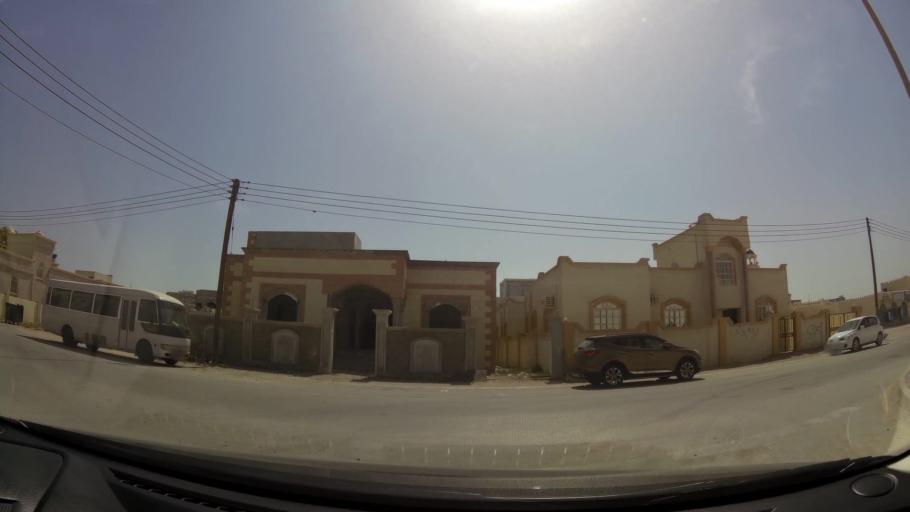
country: OM
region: Zufar
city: Salalah
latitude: 17.0473
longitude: 54.1583
